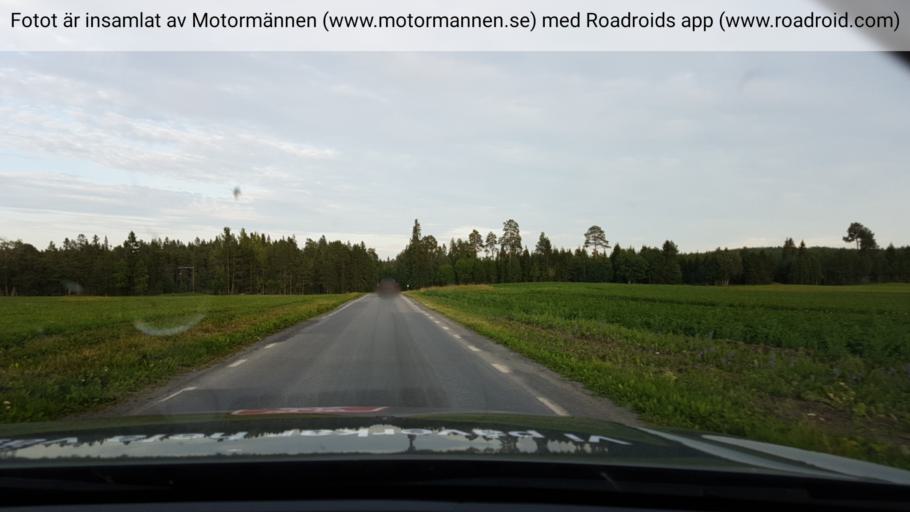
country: SE
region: Jaemtland
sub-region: Krokoms Kommun
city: Krokom
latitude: 63.1276
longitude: 14.4348
